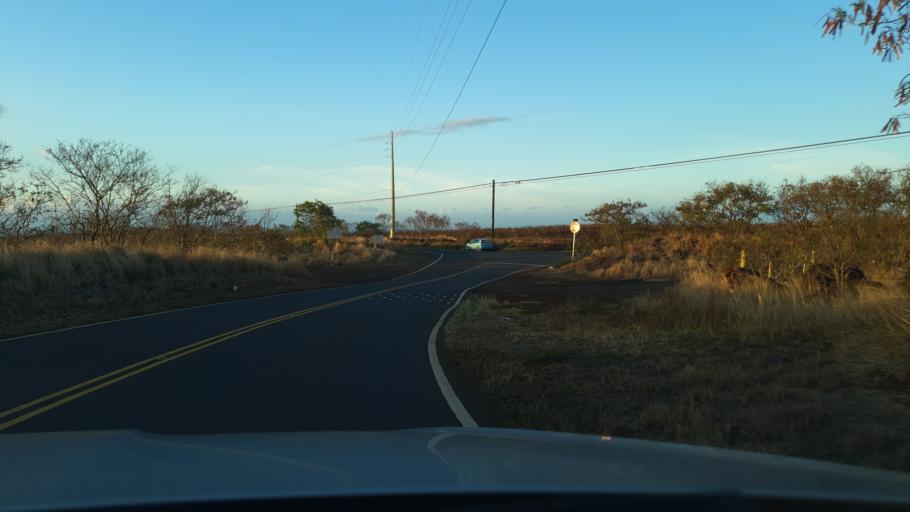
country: US
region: Hawaii
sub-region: Maui County
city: Pukalani
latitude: 20.8175
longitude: -156.3871
